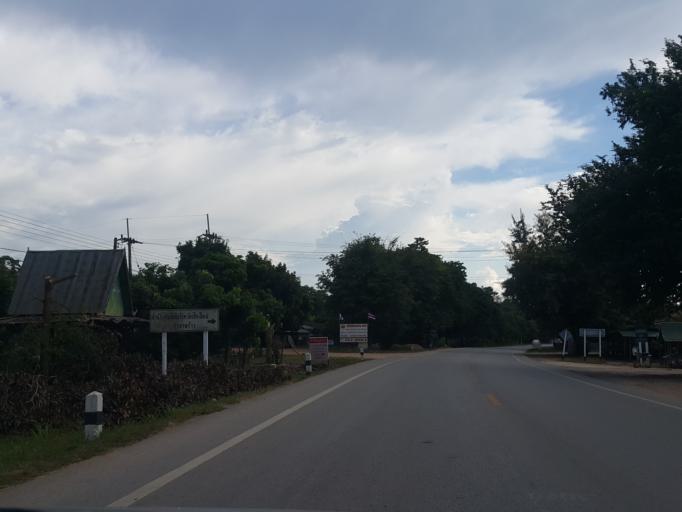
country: TH
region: Chiang Mai
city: Phrao
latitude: 19.3345
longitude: 99.1933
